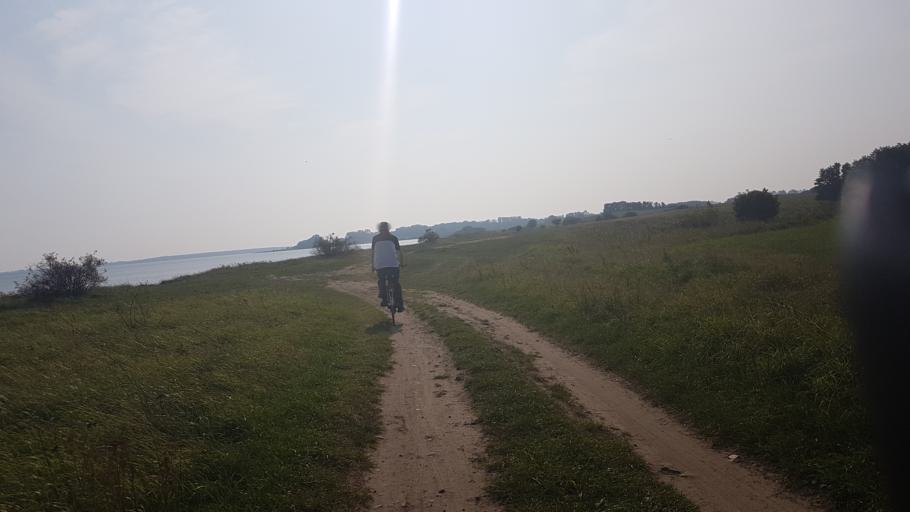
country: DE
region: Mecklenburg-Vorpommern
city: Putbus
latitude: 54.3057
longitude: 13.4238
